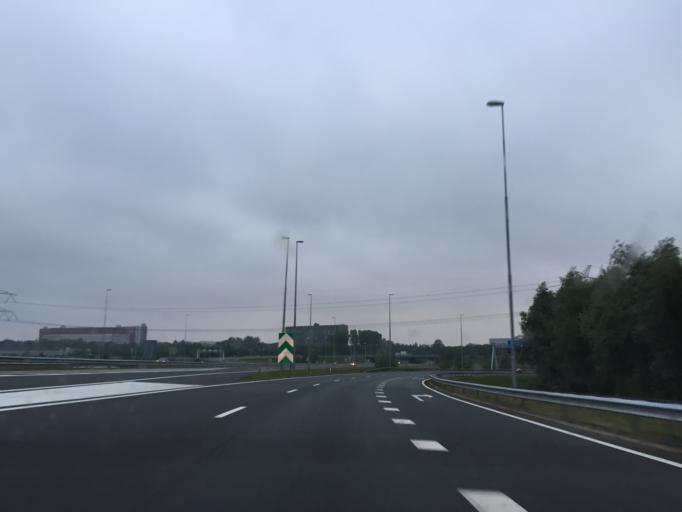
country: NL
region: North Holland
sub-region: Gemeente Zaanstad
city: Zaandam
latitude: 52.4590
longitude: 4.8465
